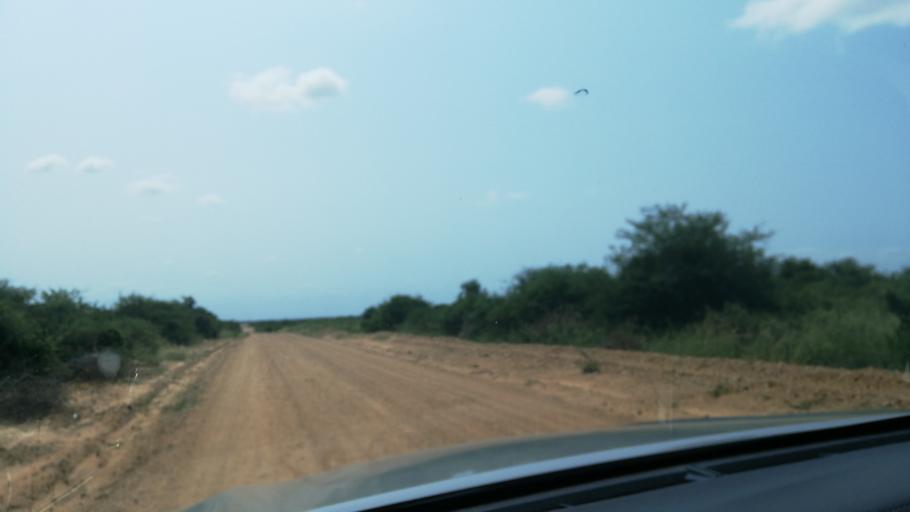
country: MZ
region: Maputo
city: Matola
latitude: -26.0835
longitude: 32.3914
